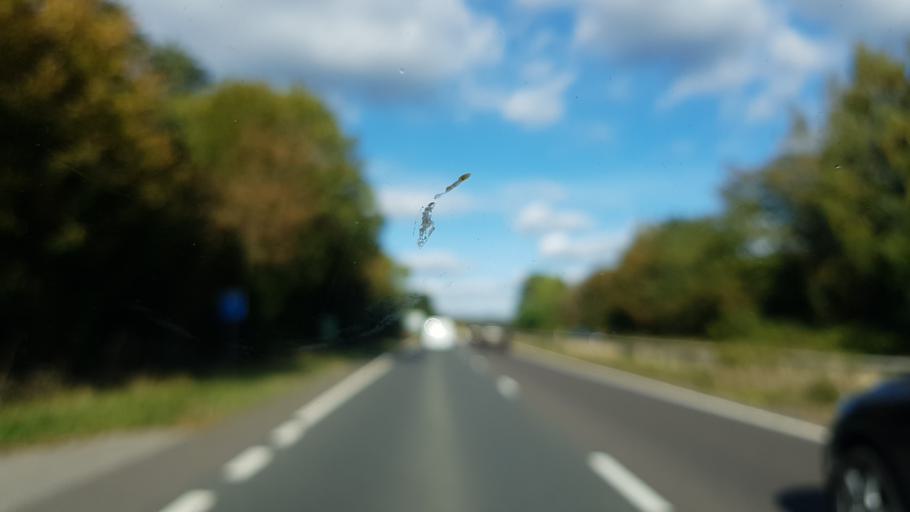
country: GB
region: England
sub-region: Surrey
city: Milford
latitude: 51.2119
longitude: -0.6496
